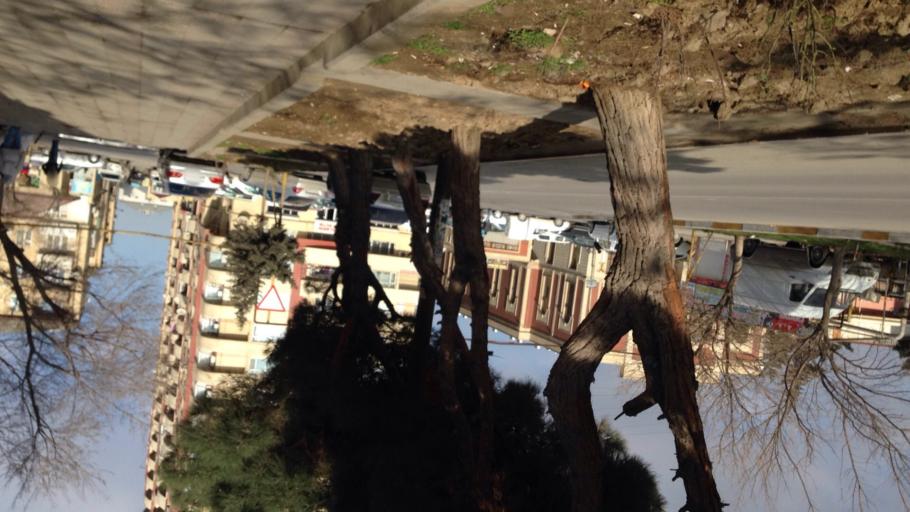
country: AZ
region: Baki
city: Baku
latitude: 40.4093
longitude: 49.8670
